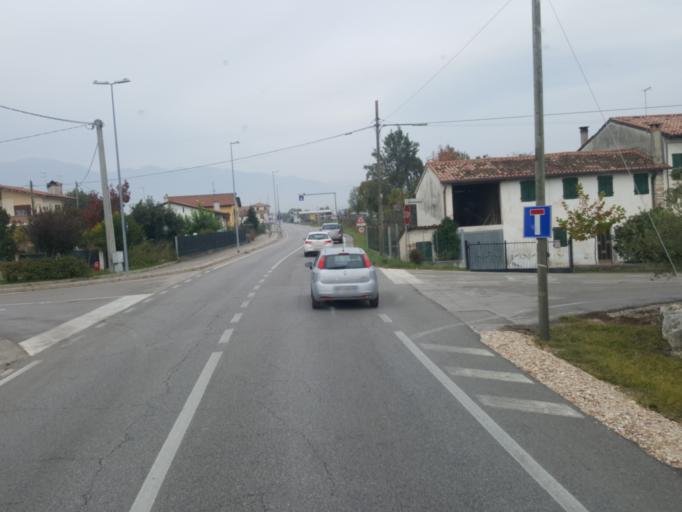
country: IT
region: Veneto
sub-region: Provincia di Treviso
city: Loria Bessica
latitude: 45.7376
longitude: 11.8664
